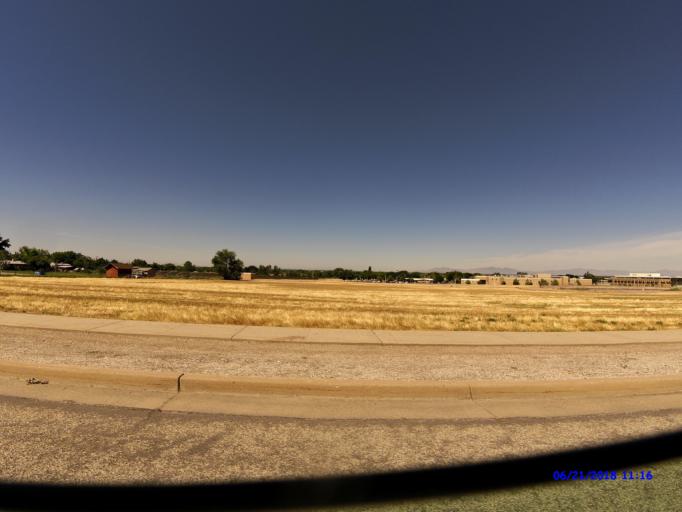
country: US
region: Utah
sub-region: Weber County
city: Harrisville
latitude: 41.2631
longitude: -111.9582
